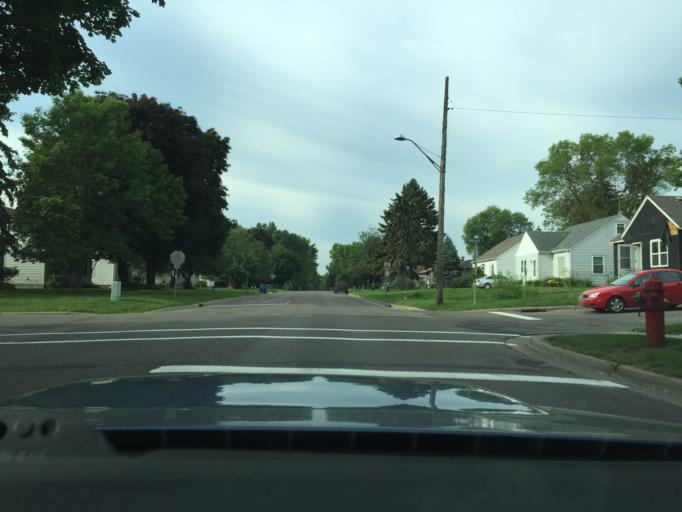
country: US
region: Minnesota
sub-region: Dakota County
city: West Saint Paul
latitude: 44.9091
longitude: -93.1018
